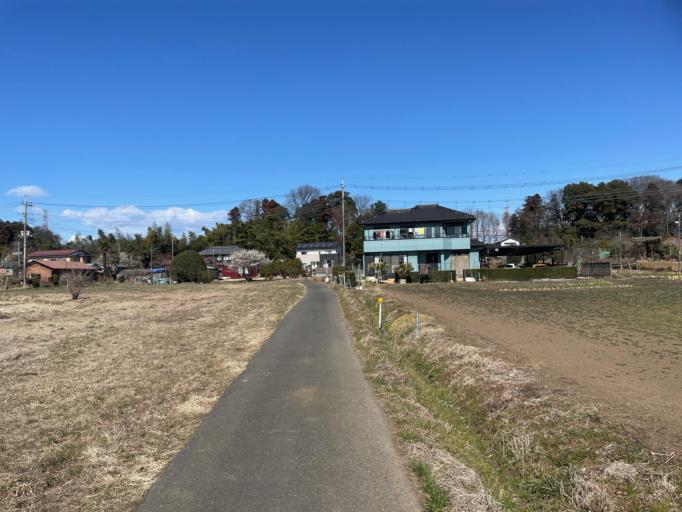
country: JP
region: Saitama
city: Sakado
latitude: 35.9531
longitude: 139.4366
